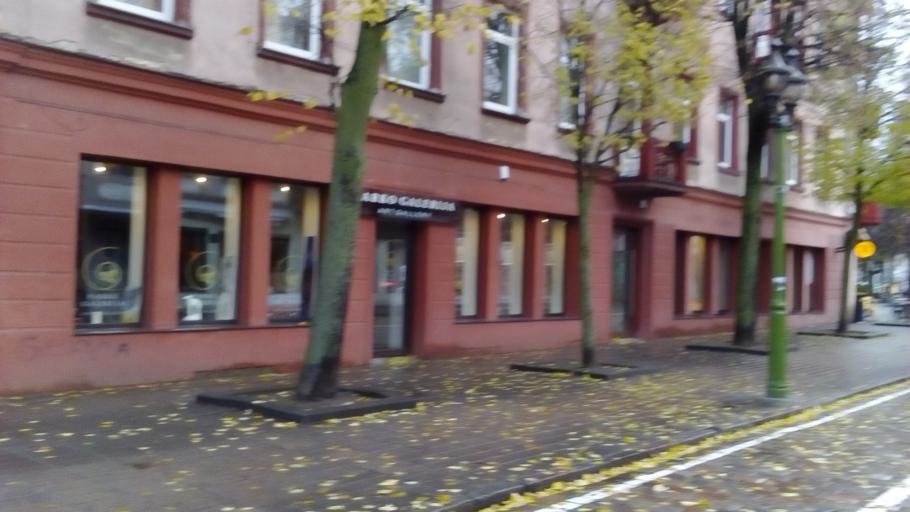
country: LT
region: Kauno apskritis
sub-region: Kaunas
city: Kaunas
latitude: 54.8969
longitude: 23.8975
